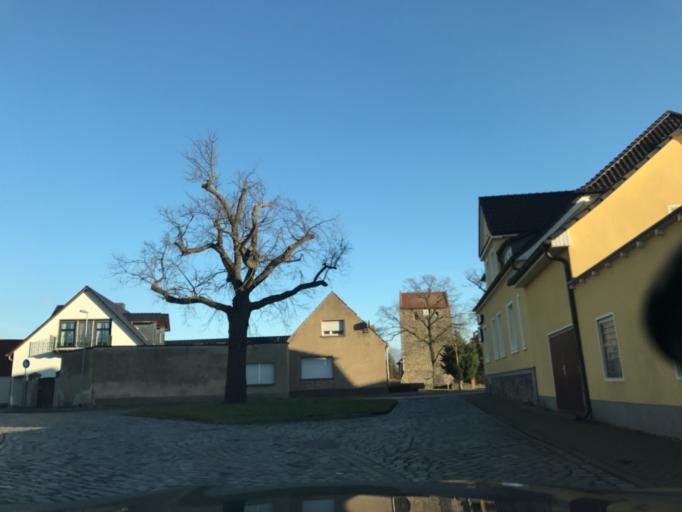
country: DE
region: Saxony-Anhalt
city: Mockern
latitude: 52.1531
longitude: 11.9491
